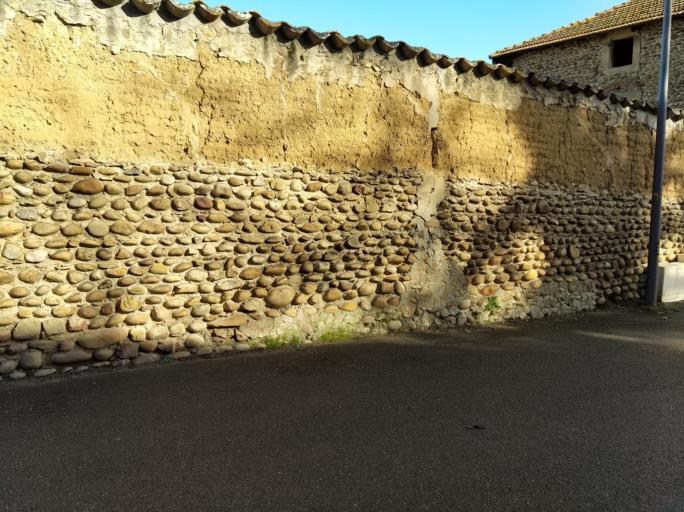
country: FR
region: Rhone-Alpes
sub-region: Departement de la Drome
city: Saint-Sorlin-en-Valloire
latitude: 45.2910
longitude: 4.9957
